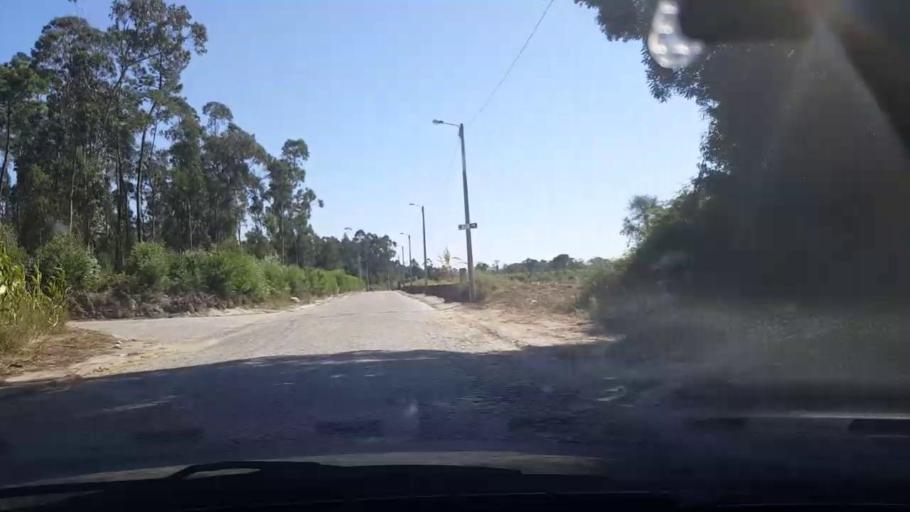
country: PT
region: Porto
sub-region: Vila do Conde
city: Arvore
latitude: 41.3163
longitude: -8.6894
